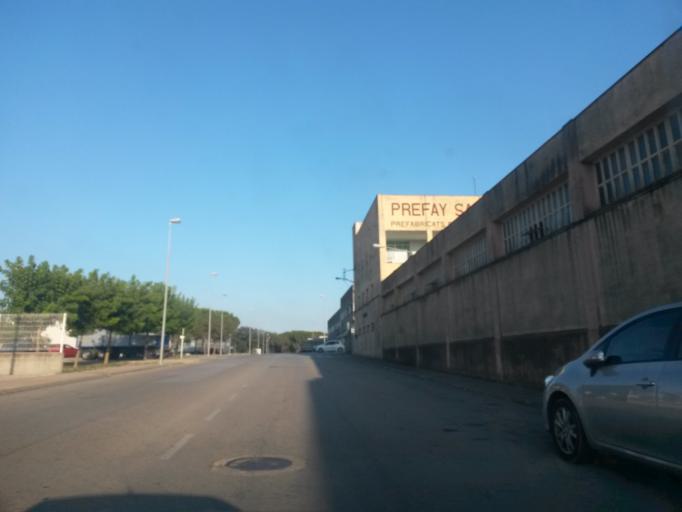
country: ES
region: Catalonia
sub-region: Provincia de Girona
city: Fornells de la Selva
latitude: 41.9347
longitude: 2.8005
